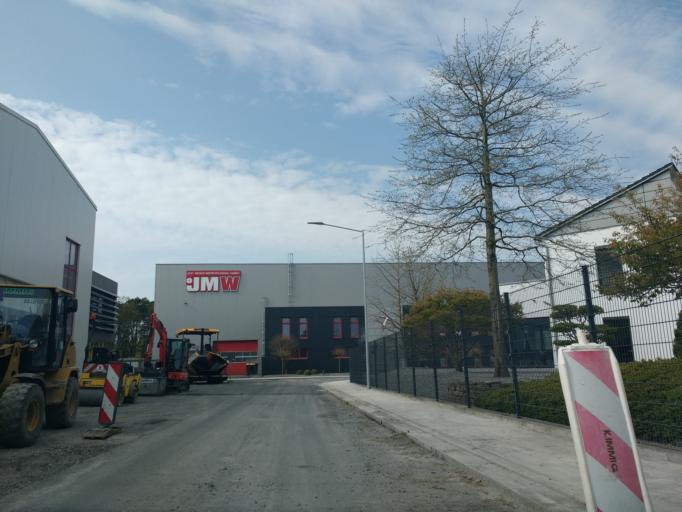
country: DE
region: North Rhine-Westphalia
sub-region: Regierungsbezirk Detmold
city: Hovelhof
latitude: 51.8365
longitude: 8.6482
